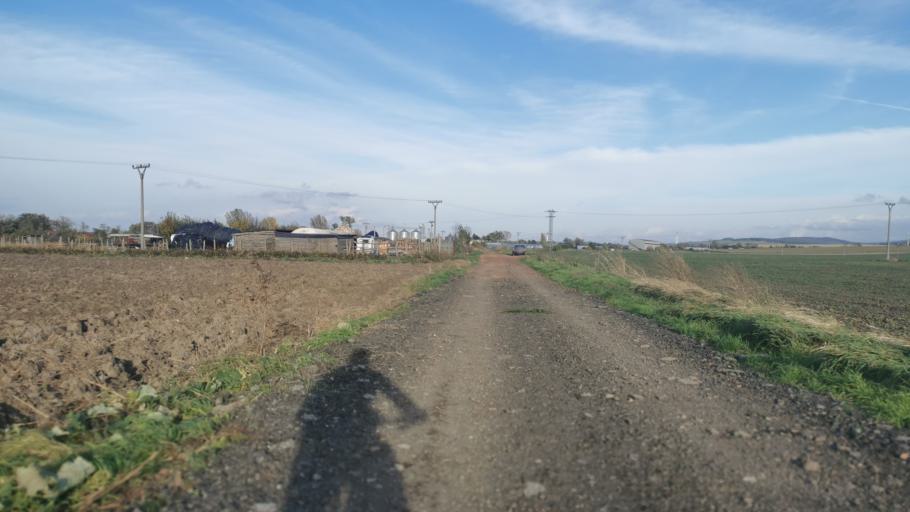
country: SK
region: Trnavsky
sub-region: Okres Skalica
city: Skalica
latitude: 48.8439
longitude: 17.2445
